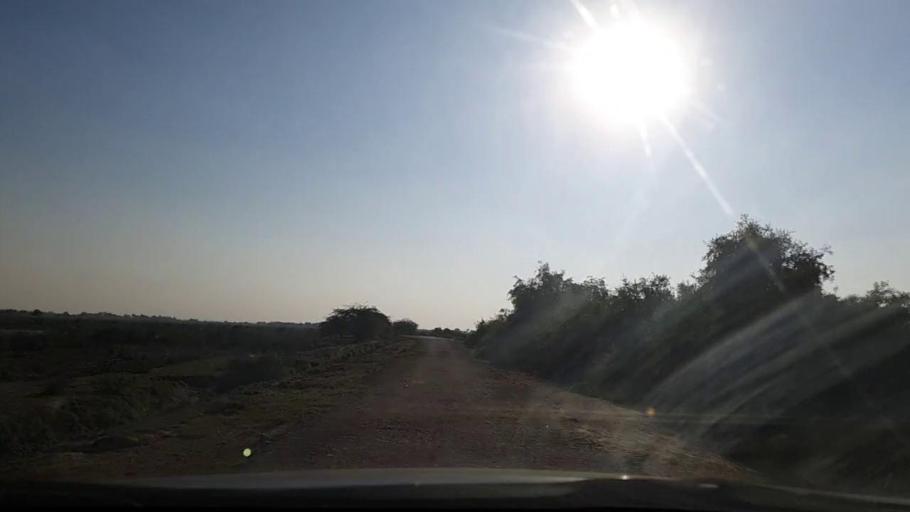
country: PK
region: Sindh
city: Mirpur Sakro
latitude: 24.5129
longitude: 67.6316
